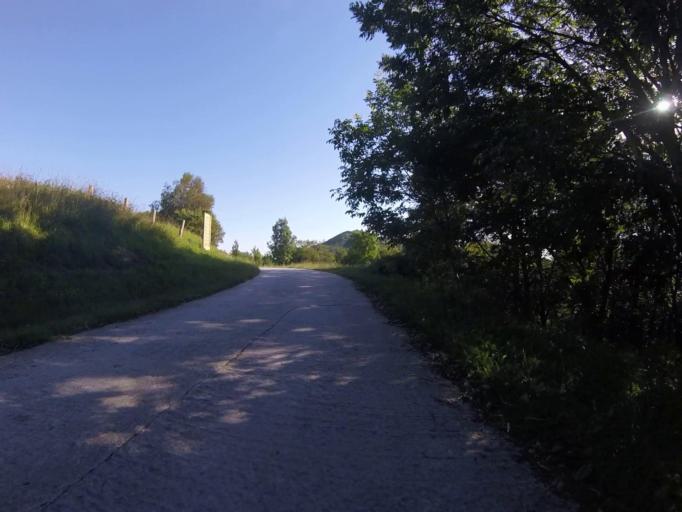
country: ES
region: Basque Country
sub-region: Provincia de Guipuzcoa
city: Fuenterrabia
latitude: 43.3704
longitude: -1.8197
